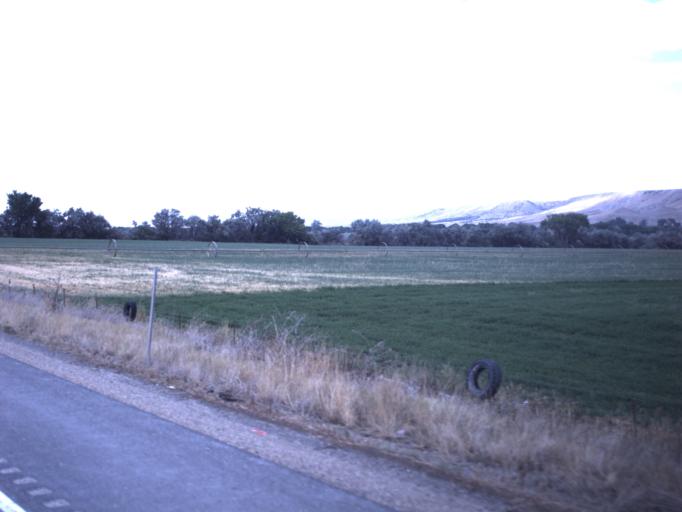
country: US
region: Utah
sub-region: Duchesne County
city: Duchesne
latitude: 40.1536
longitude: -110.2253
